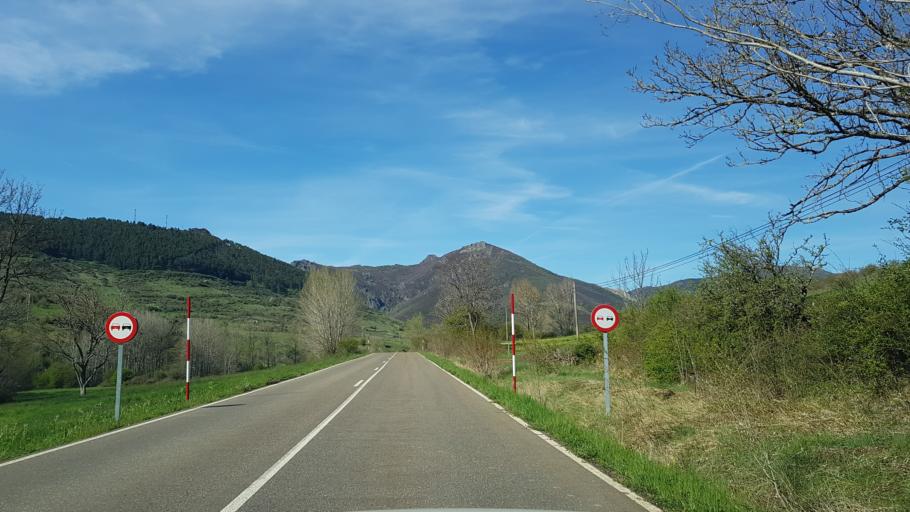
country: ES
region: Castille and Leon
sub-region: Provincia de Leon
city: Villamanin
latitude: 42.9459
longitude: -5.6389
